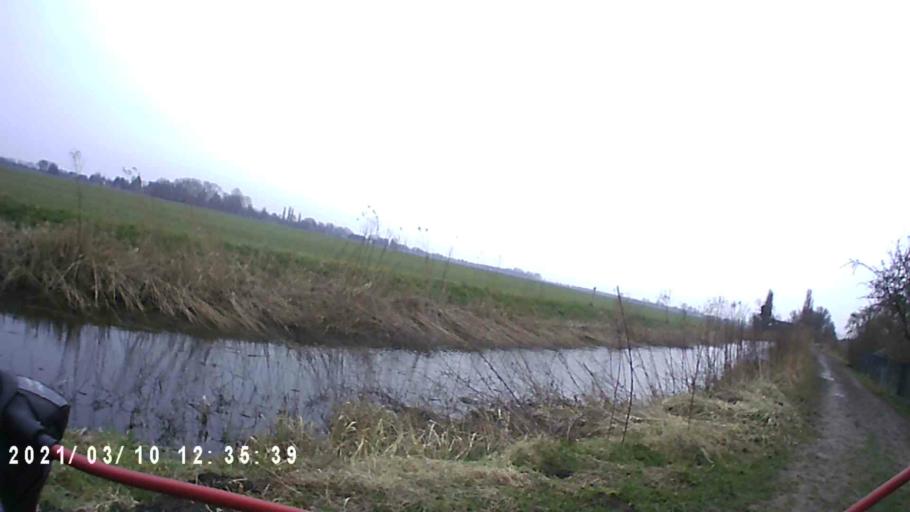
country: NL
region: Groningen
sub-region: Gemeente Groningen
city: Oosterpark
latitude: 53.2484
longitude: 6.6365
